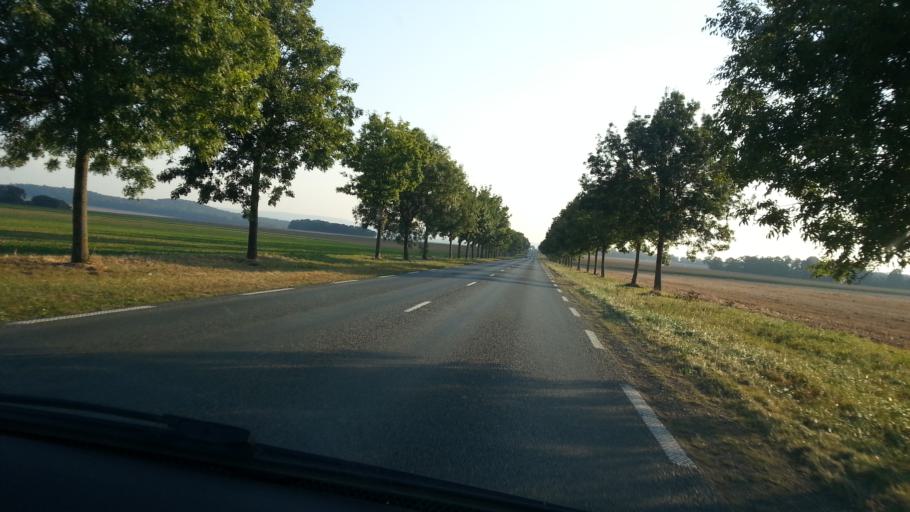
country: FR
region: Picardie
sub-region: Departement de l'Oise
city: Estrees-Saint-Denis
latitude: 49.4002
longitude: 2.6253
